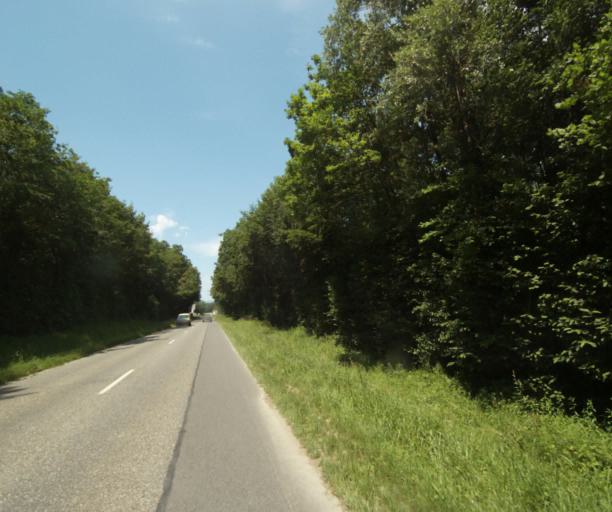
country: FR
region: Rhone-Alpes
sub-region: Departement de la Haute-Savoie
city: Douvaine
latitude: 46.3182
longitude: 6.2970
